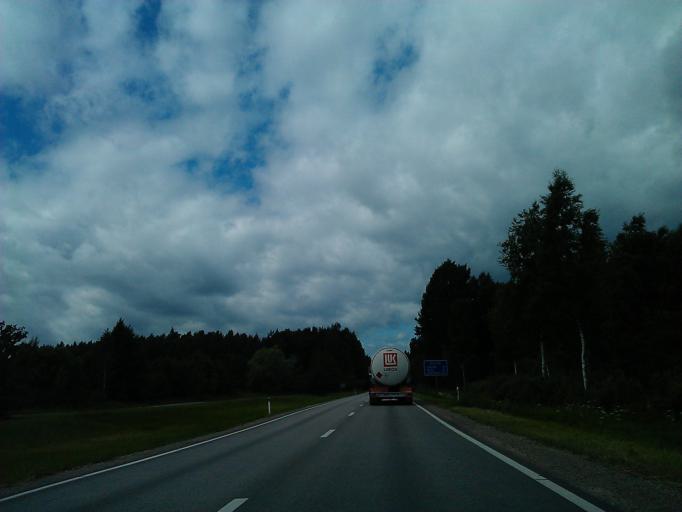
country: LV
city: Tireli
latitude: 56.9285
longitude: 23.5795
